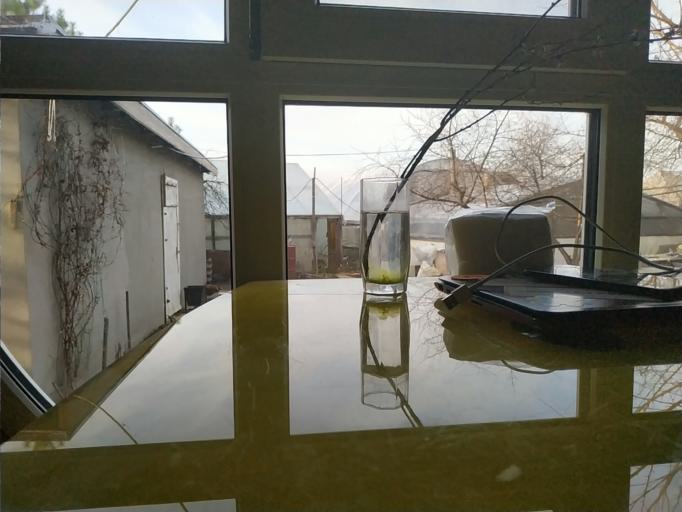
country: RU
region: Republic of Karelia
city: Suoyarvi
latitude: 62.0304
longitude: 32.1958
